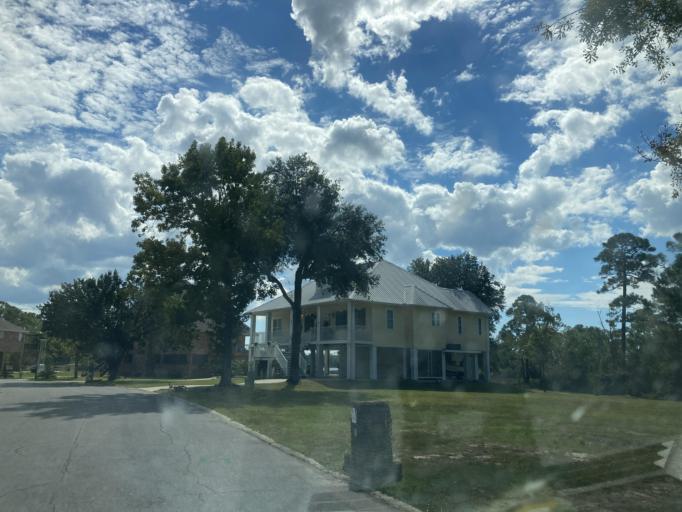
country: US
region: Mississippi
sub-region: Jackson County
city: Gulf Hills
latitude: 30.4374
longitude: -88.8515
